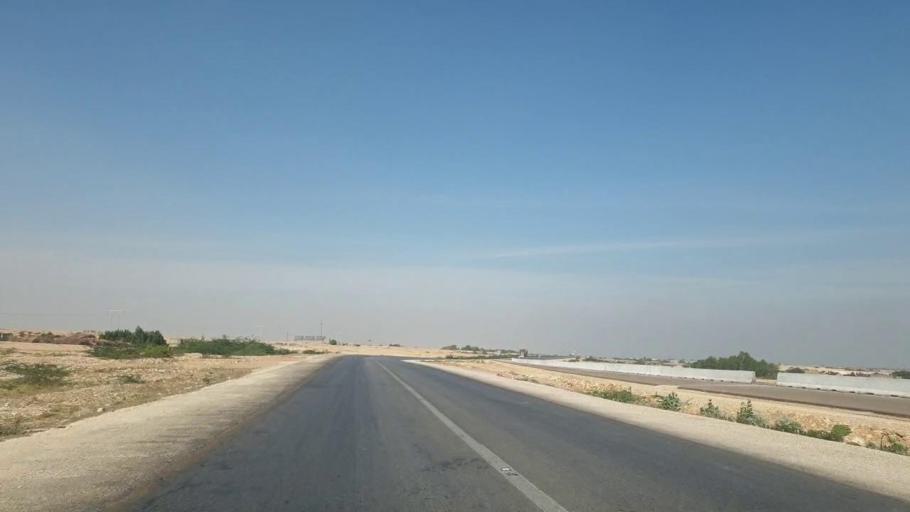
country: PK
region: Sindh
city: Matiari
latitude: 25.6839
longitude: 68.2957
